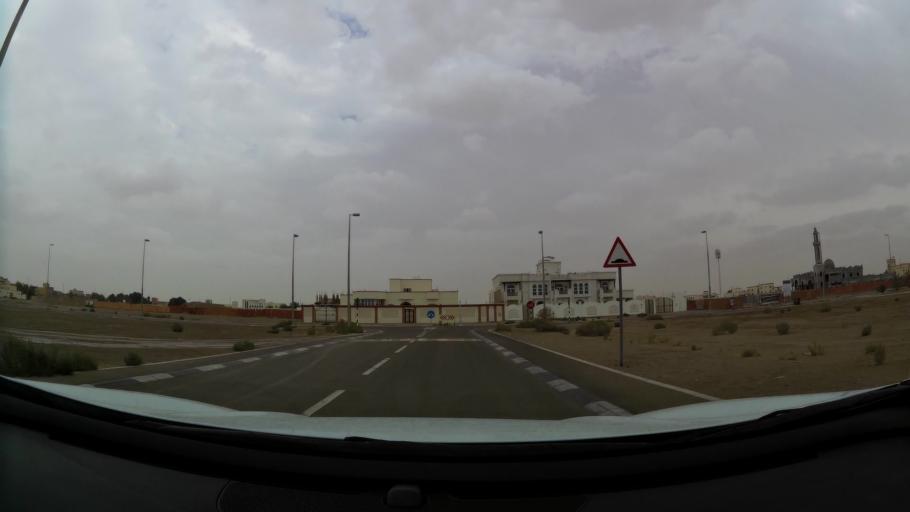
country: AE
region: Abu Dhabi
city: Abu Dhabi
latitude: 24.3540
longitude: 54.6570
